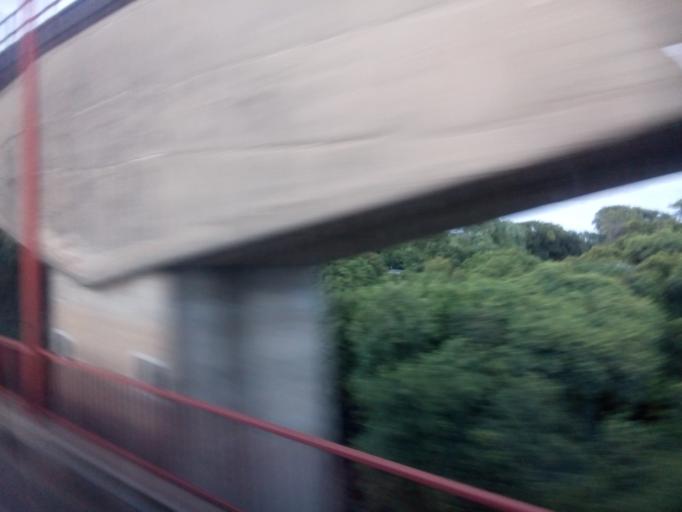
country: AR
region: Buenos Aires
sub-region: Partido de Zarate
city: Zarate
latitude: -34.1146
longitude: -59.0076
